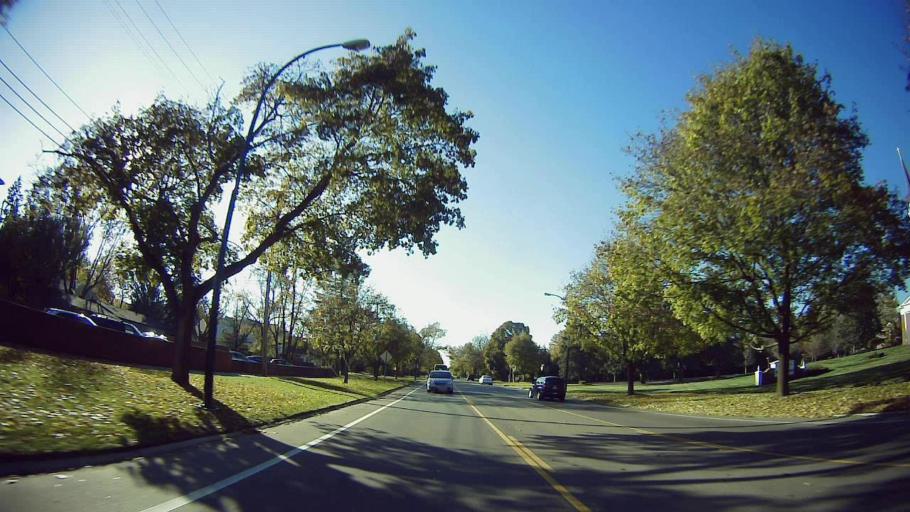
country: US
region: Michigan
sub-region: Oakland County
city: Beverly Hills
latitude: 42.5460
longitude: -83.2378
